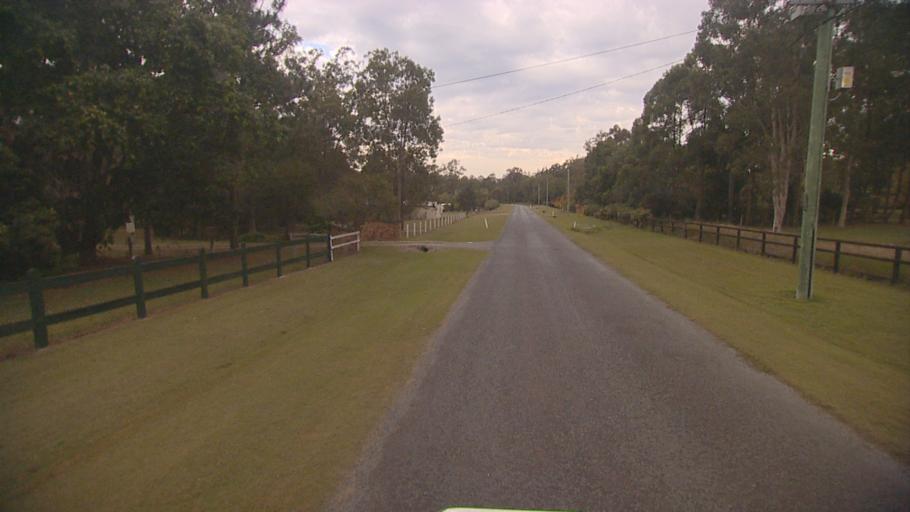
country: AU
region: Queensland
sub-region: Logan
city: Chambers Flat
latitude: -27.7913
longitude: 153.1111
